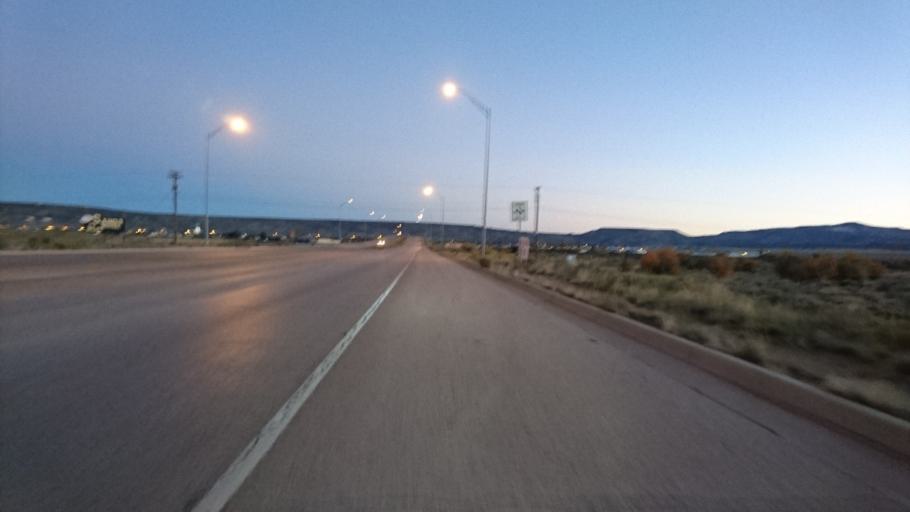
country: US
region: New Mexico
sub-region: Cibola County
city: Grants
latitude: 35.1323
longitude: -107.8272
